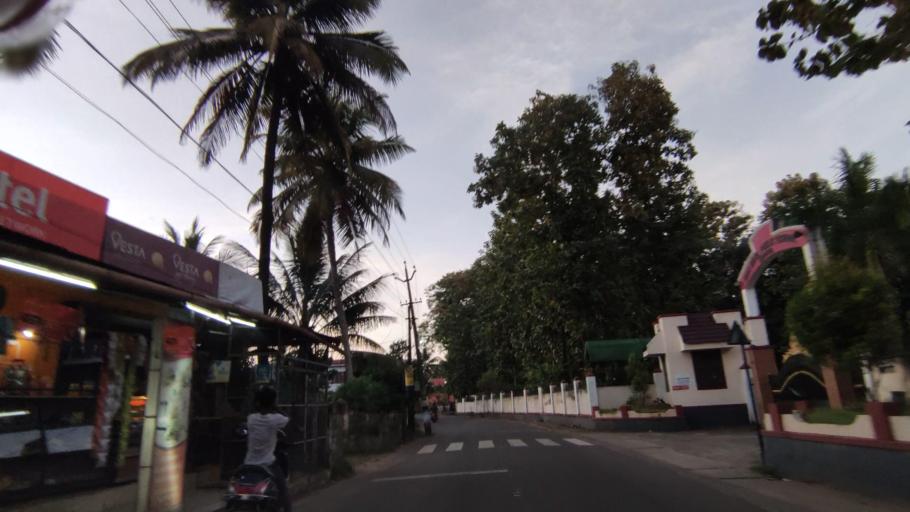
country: IN
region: Kerala
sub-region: Kottayam
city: Kottayam
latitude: 9.6694
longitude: 76.5064
